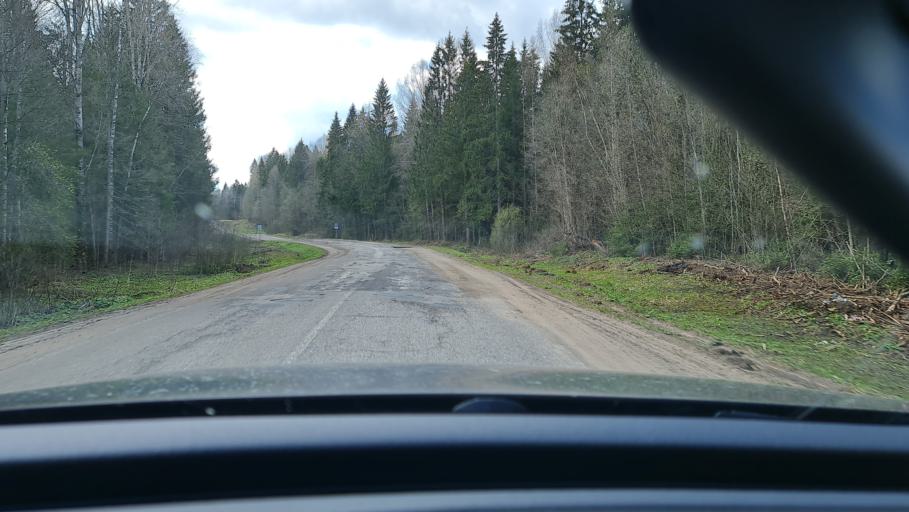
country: RU
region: Tverskaya
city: Toropets
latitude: 56.6264
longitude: 31.4332
